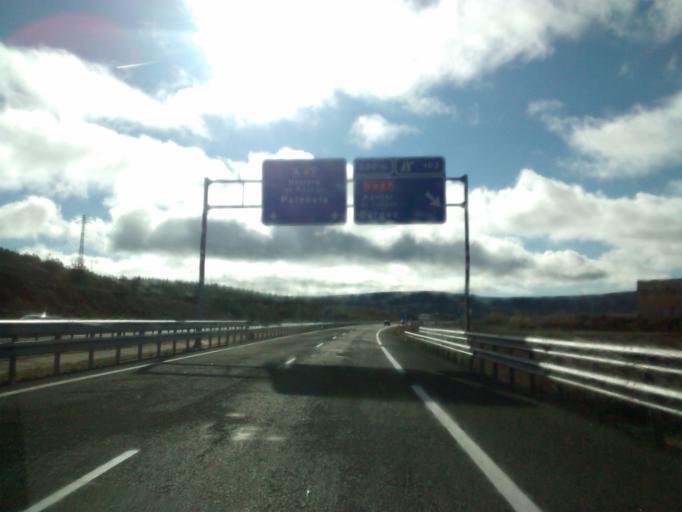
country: ES
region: Castille and Leon
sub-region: Provincia de Palencia
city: Aguilar de Campoo
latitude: 42.7927
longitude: -4.2369
